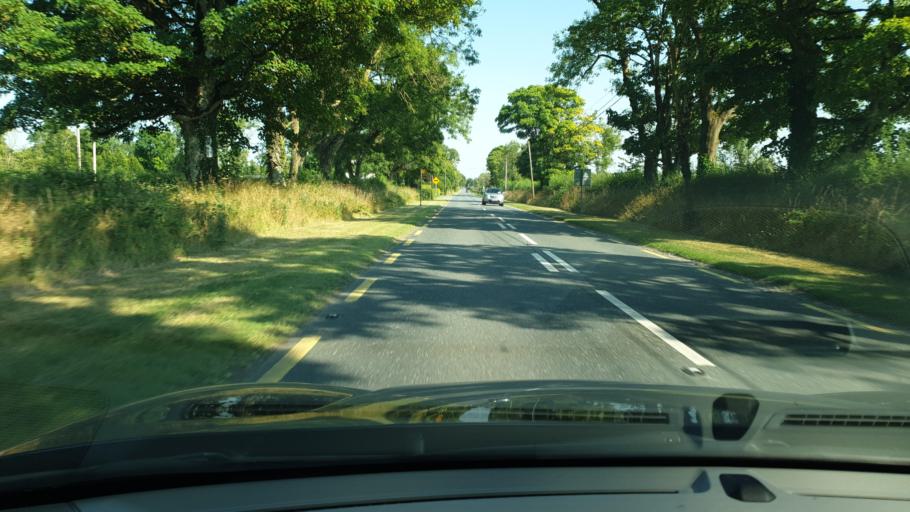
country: IE
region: Leinster
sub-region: An Mhi
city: Athboy
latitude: 53.6454
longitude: -6.8556
